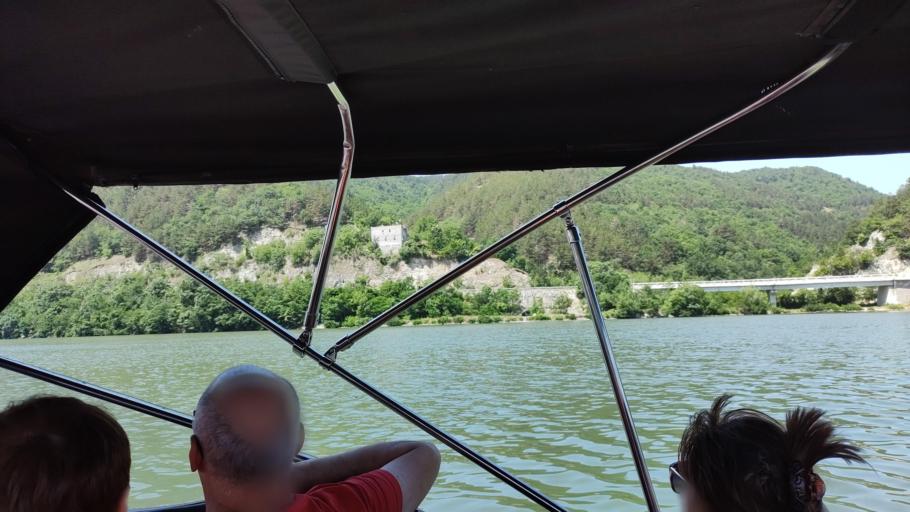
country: RO
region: Mehedinti
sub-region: Comuna Svinita
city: Svinita
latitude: 44.5284
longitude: 22.2063
